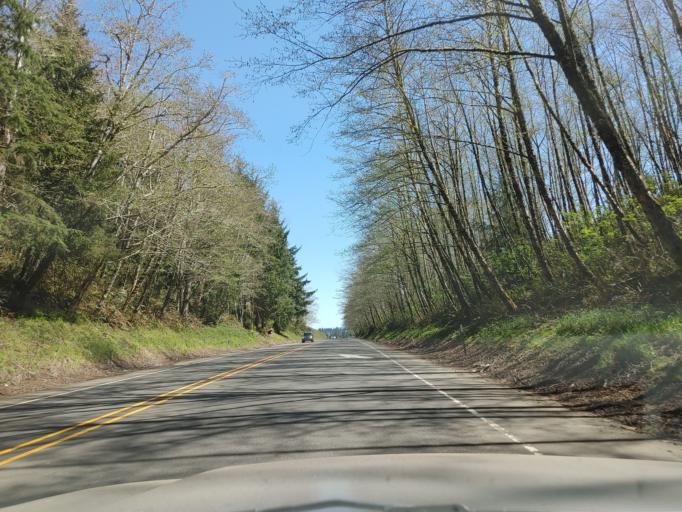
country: US
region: Oregon
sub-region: Clatsop County
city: Warrenton
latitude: 46.1439
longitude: -123.8920
